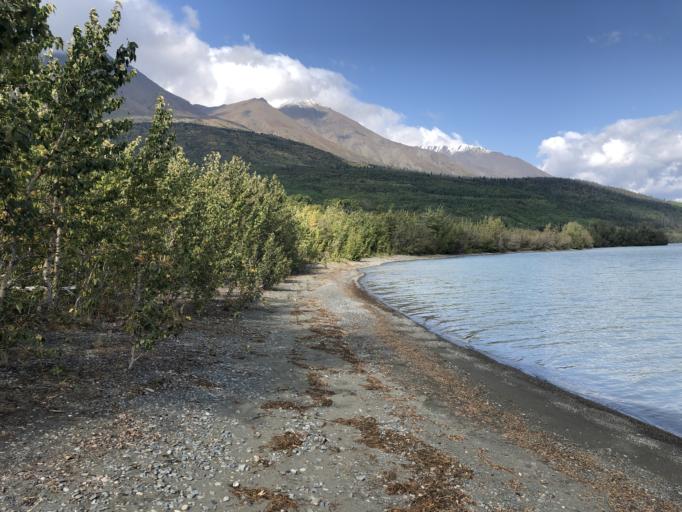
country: CA
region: Yukon
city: Haines Junction
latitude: 60.3977
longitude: -137.0425
